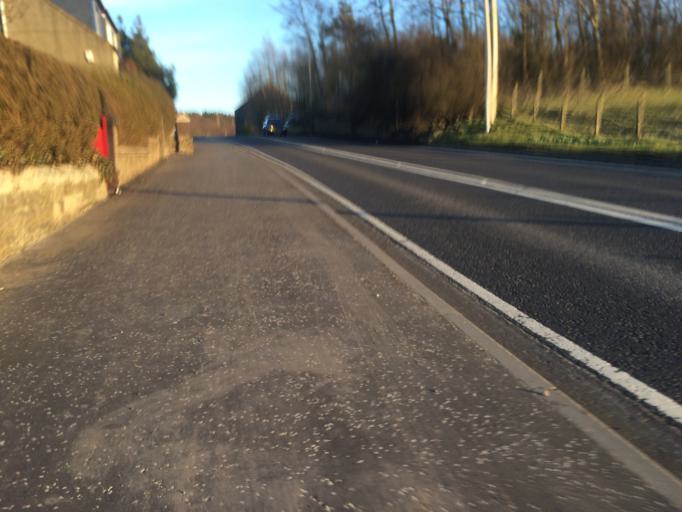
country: GB
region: Scotland
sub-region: Fife
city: Lochgelly
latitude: 56.1409
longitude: -3.3202
